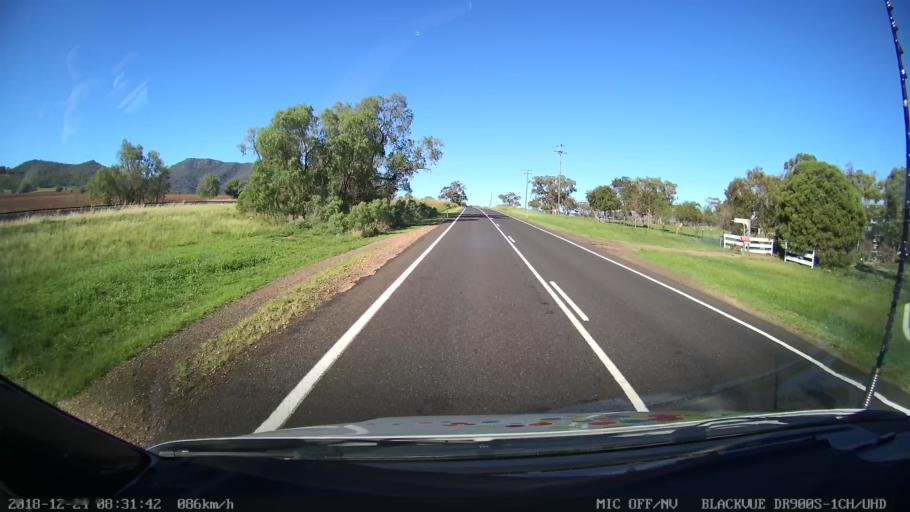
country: AU
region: New South Wales
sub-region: Tamworth Municipality
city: Phillip
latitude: -31.2752
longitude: 150.7080
